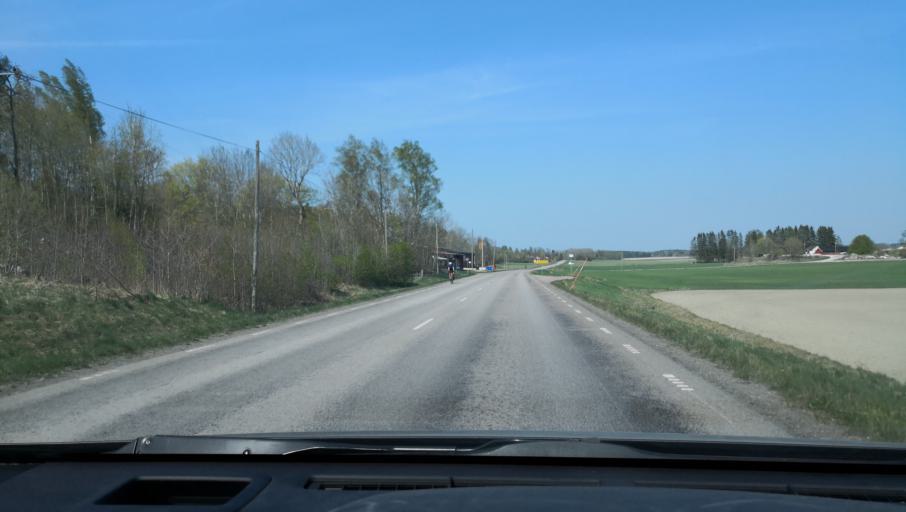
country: SE
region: Vaestmanland
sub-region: Sala Kommun
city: Sala
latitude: 59.9536
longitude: 16.6172
